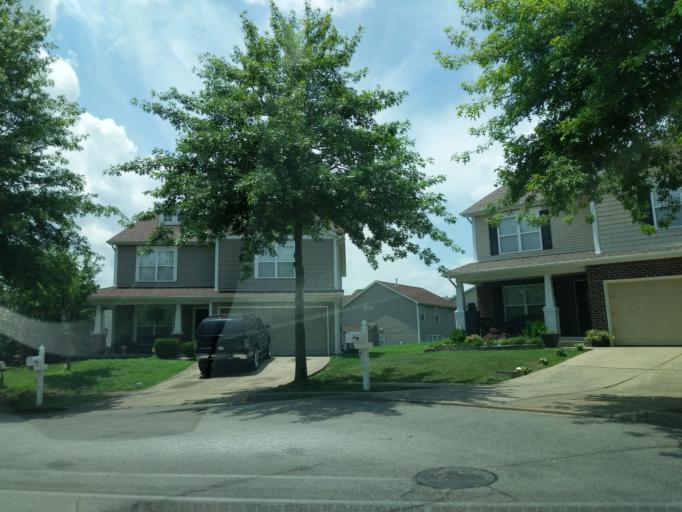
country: US
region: Tennessee
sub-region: Davidson County
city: Goodlettsville
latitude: 36.3016
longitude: -86.7255
